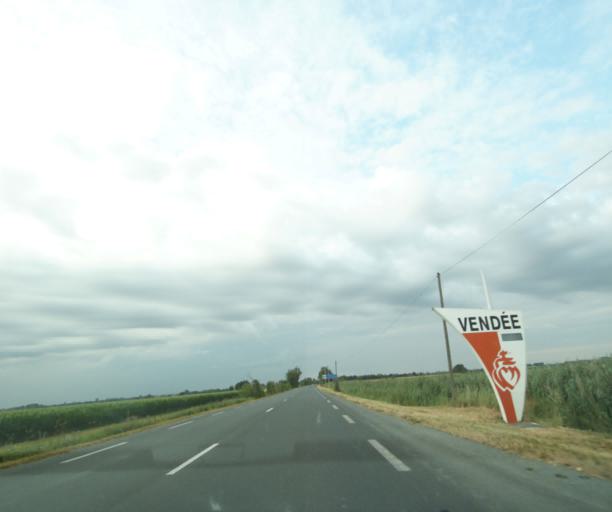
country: FR
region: Poitou-Charentes
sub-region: Departement de la Charente-Maritime
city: Marans
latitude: 46.3518
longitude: -0.9948
